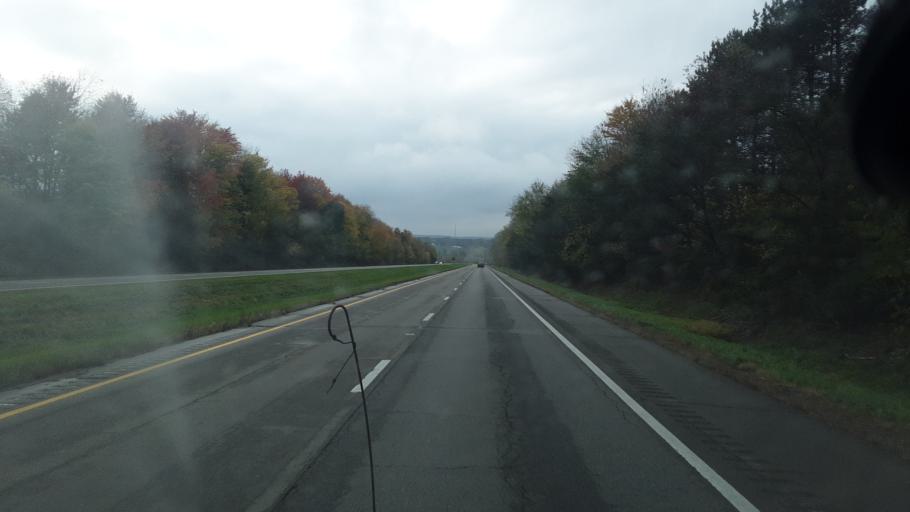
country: US
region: Ohio
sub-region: Wayne County
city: Shreve
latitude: 40.7870
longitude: -82.0845
